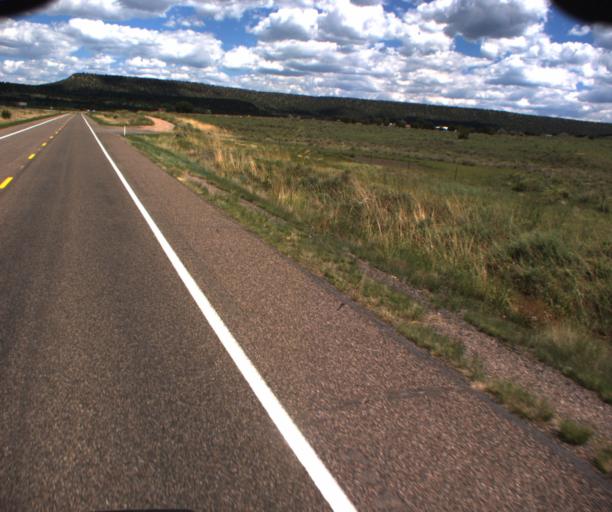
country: US
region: Arizona
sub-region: Apache County
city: Springerville
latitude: 34.1325
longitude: -109.2507
